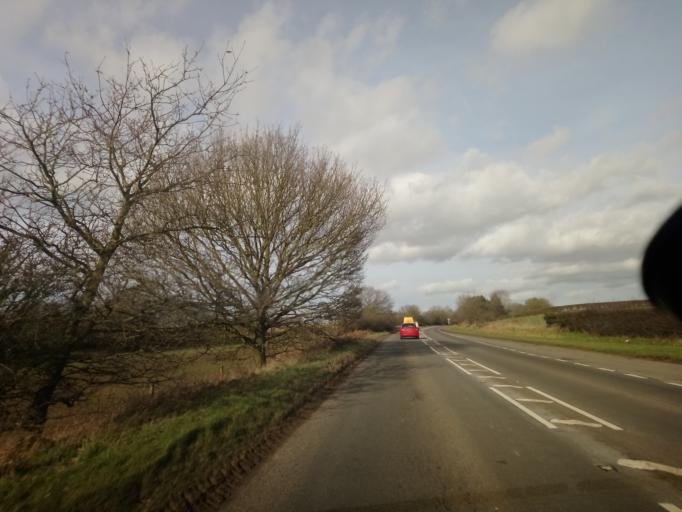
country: GB
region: England
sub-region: Telford and Wrekin
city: Eyton upon the Weald Moors
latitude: 52.7794
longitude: -2.5539
